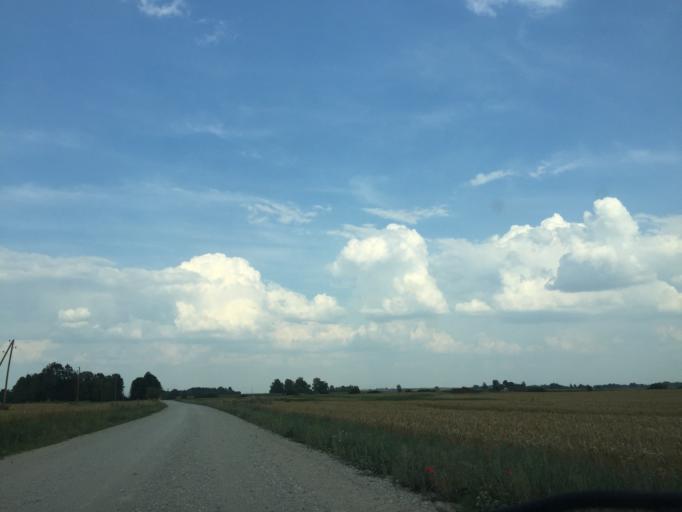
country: LT
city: Zagare
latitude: 56.4155
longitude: 23.1765
